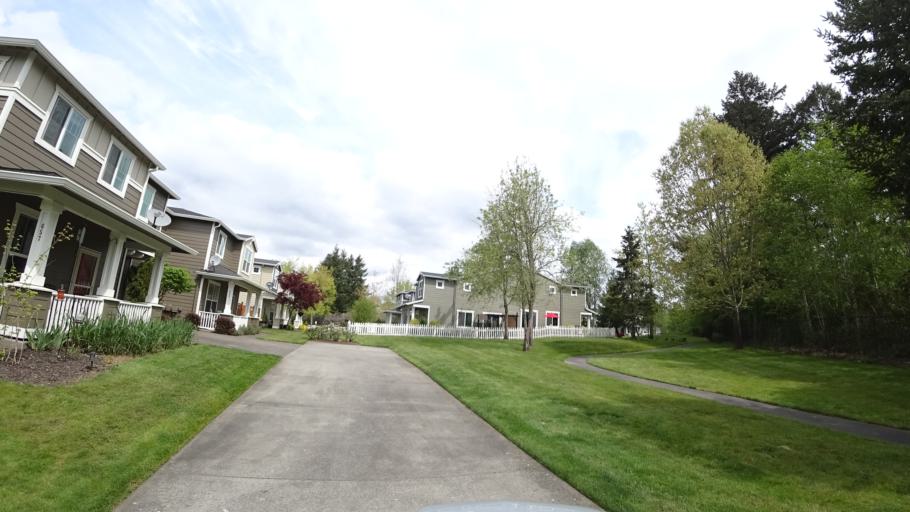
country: US
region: Oregon
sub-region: Washington County
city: Hillsboro
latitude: 45.5344
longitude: -122.9959
